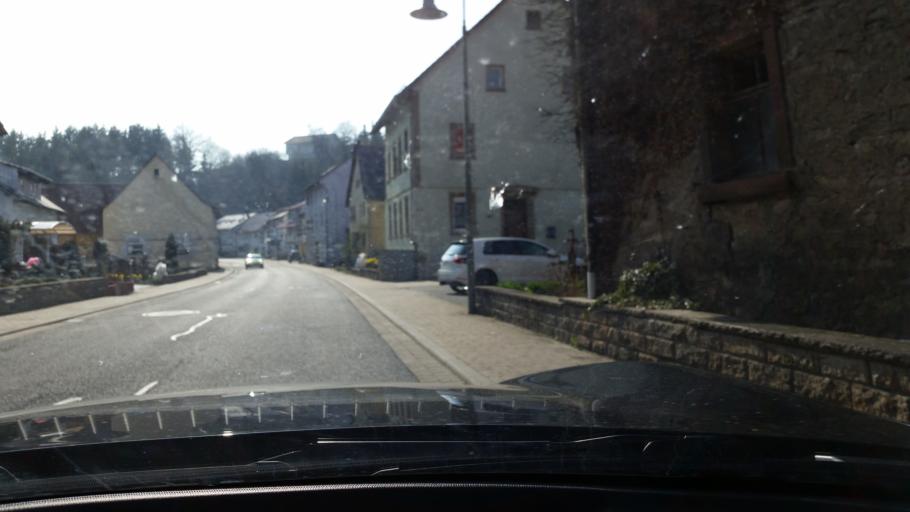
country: DE
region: Baden-Wuerttemberg
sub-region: Karlsruhe Region
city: Billigheim
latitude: 49.3724
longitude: 9.2653
